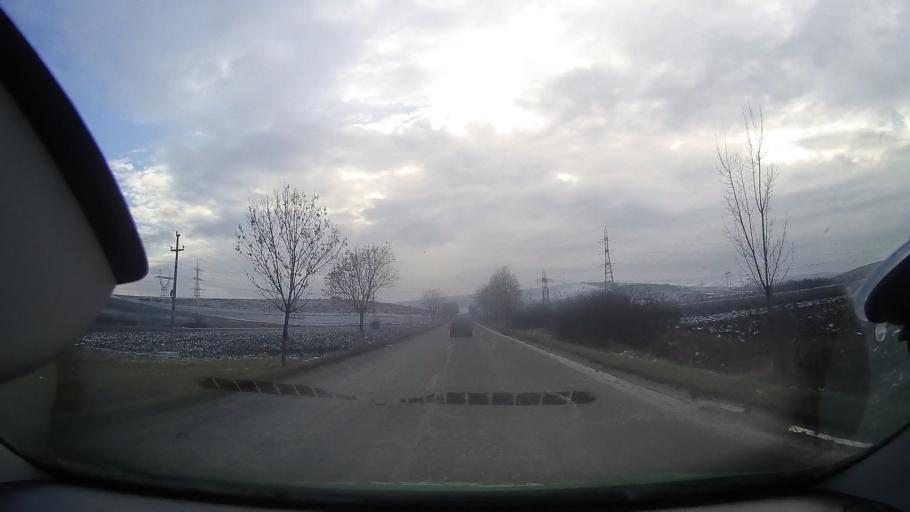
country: RO
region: Mures
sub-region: Comuna Cucerdea
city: Cucerdea
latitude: 46.4243
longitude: 24.2597
